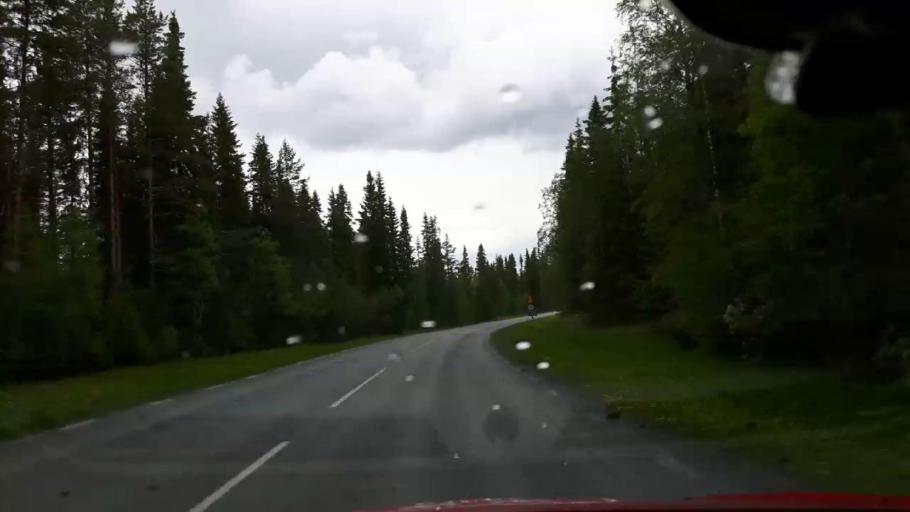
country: SE
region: Jaemtland
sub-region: Krokoms Kommun
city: Krokom
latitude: 63.4116
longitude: 14.2395
